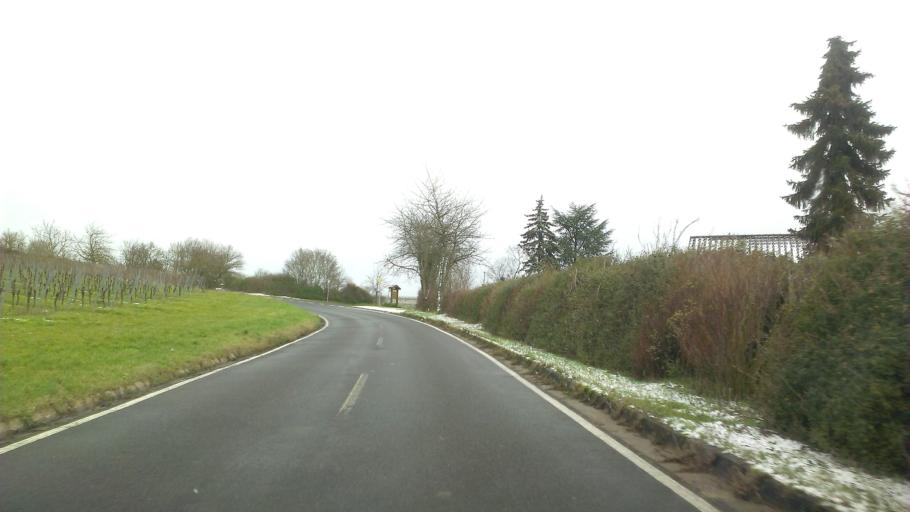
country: DE
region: Rheinland-Pfalz
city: Monsheim
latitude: 49.6400
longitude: 8.2252
